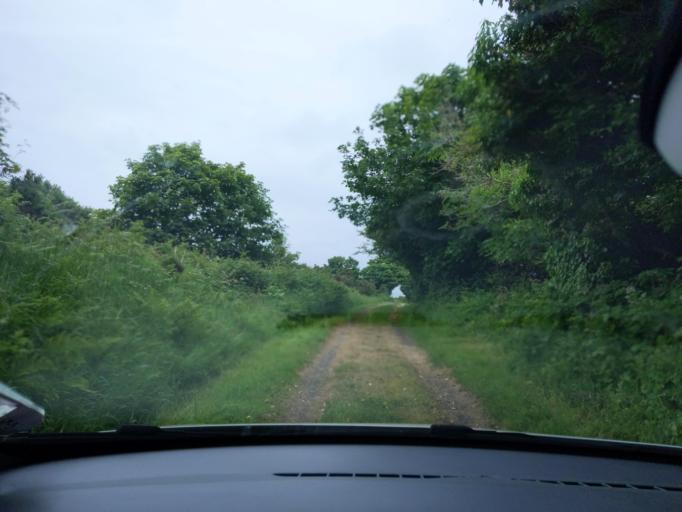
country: IM
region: Castletown
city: Castletown
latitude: 54.1152
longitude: -4.5912
